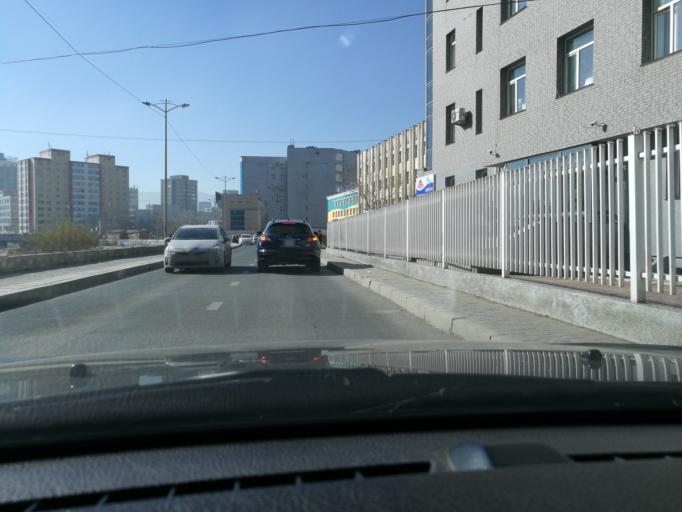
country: MN
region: Ulaanbaatar
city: Ulaanbaatar
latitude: 47.9199
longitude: 106.9305
